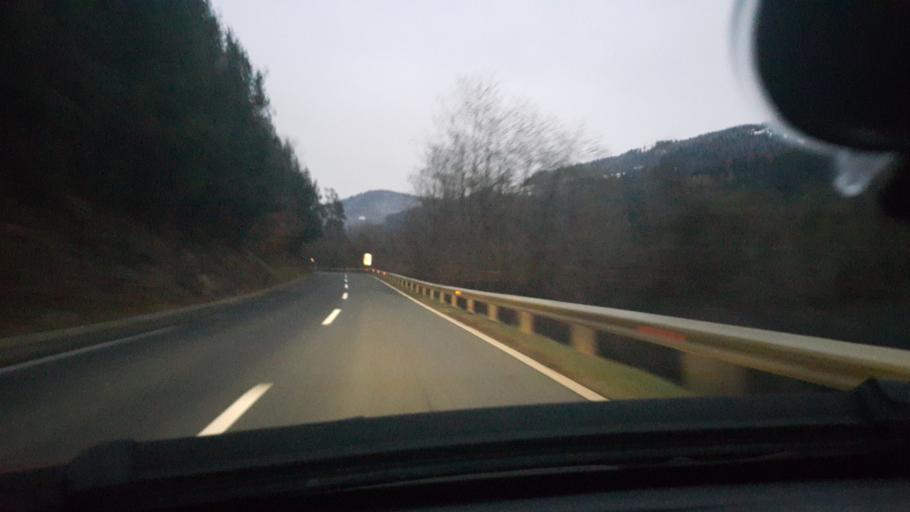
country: AT
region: Carinthia
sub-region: Politischer Bezirk Wolfsberg
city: Lavamund
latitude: 46.6103
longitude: 14.9762
